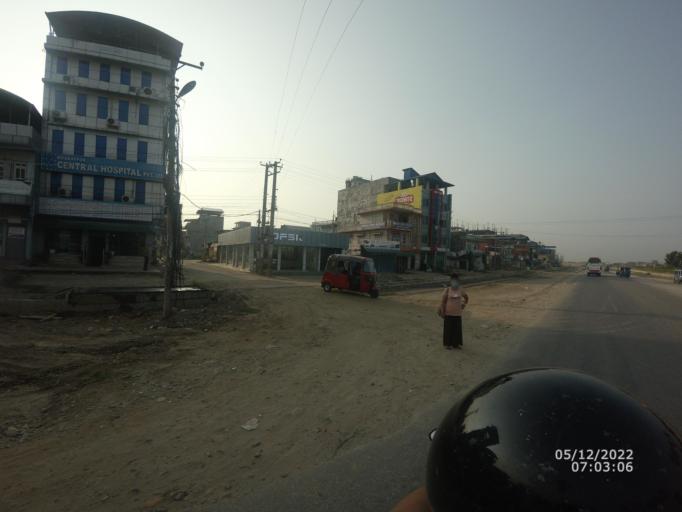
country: NP
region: Central Region
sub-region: Narayani Zone
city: Bharatpur
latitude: 27.6784
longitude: 84.4306
